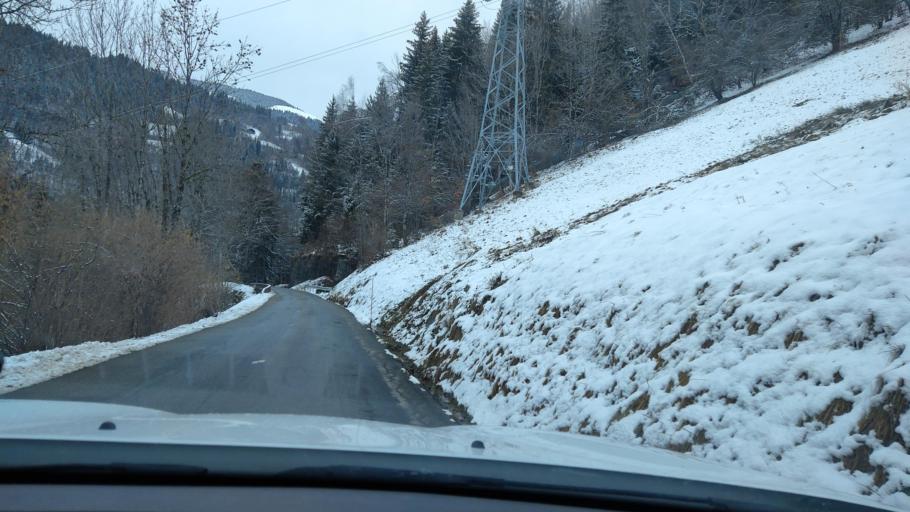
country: FR
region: Rhone-Alpes
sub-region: Departement de la Savoie
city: Beaufort
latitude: 45.7297
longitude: 6.5738
